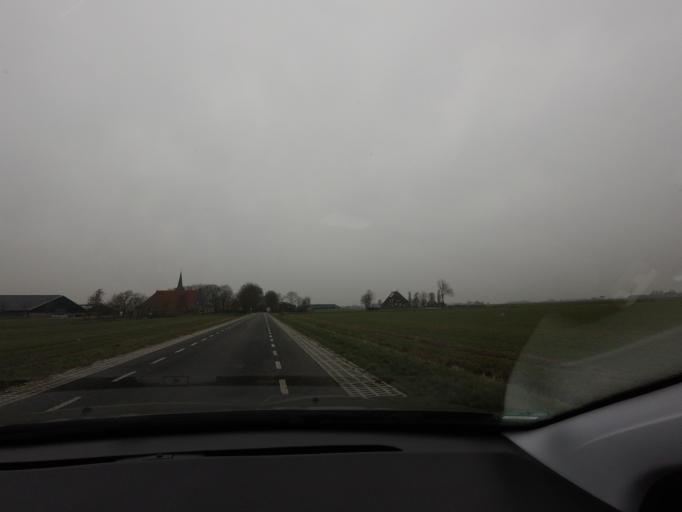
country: NL
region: Friesland
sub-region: Sudwest Fryslan
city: Bolsward
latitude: 53.1082
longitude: 5.5404
